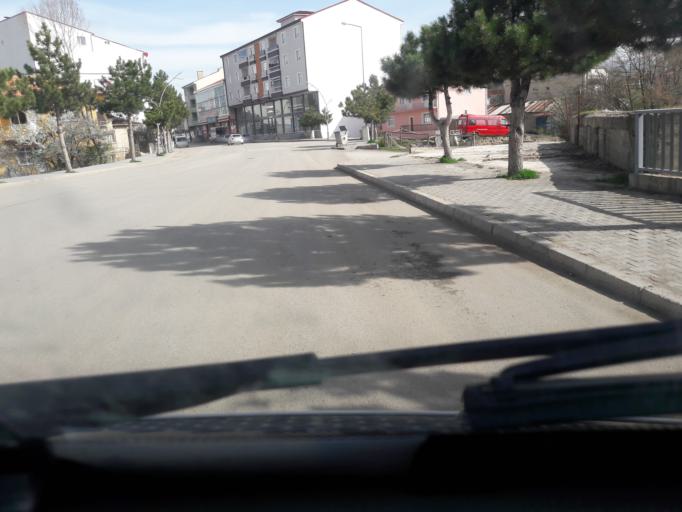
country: TR
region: Gumushane
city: Kelkit
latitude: 40.1352
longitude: 39.4339
